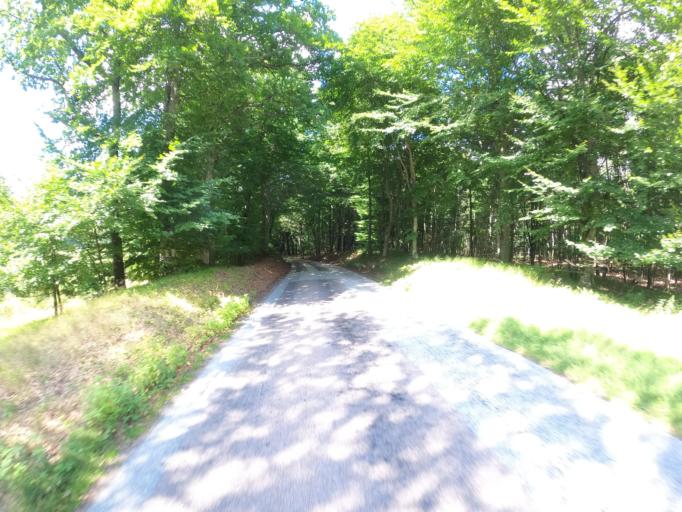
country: SE
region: Skane
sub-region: Lunds Kommun
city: Veberod
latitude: 55.5821
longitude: 13.4638
